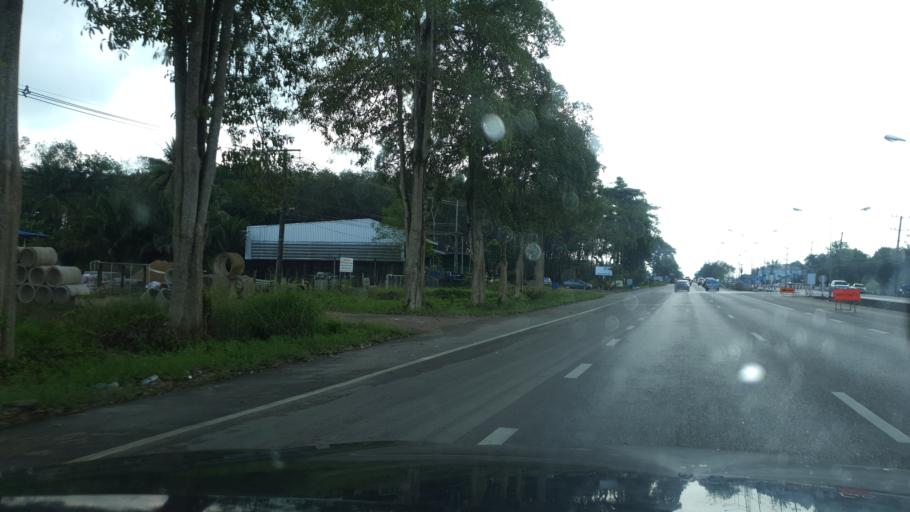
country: TH
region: Chumphon
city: Tha Sae
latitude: 10.7360
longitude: 99.2063
